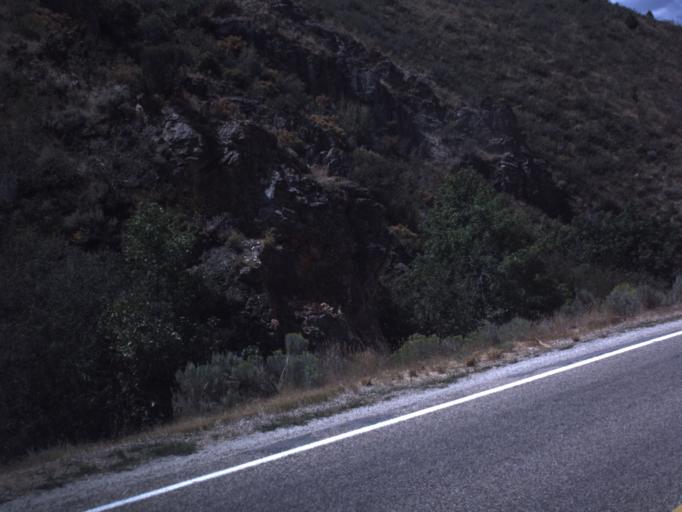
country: US
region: Utah
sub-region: Rich County
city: Randolph
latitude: 41.8241
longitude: -111.2978
